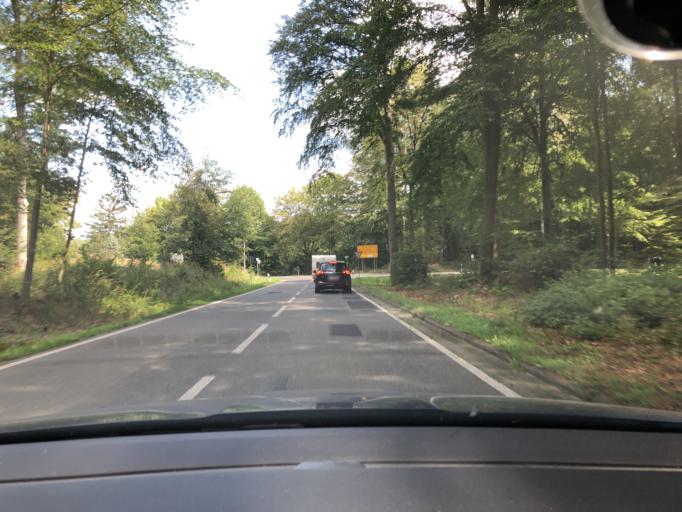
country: DE
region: Brandenburg
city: Neuruppin
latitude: 53.0333
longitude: 12.7596
